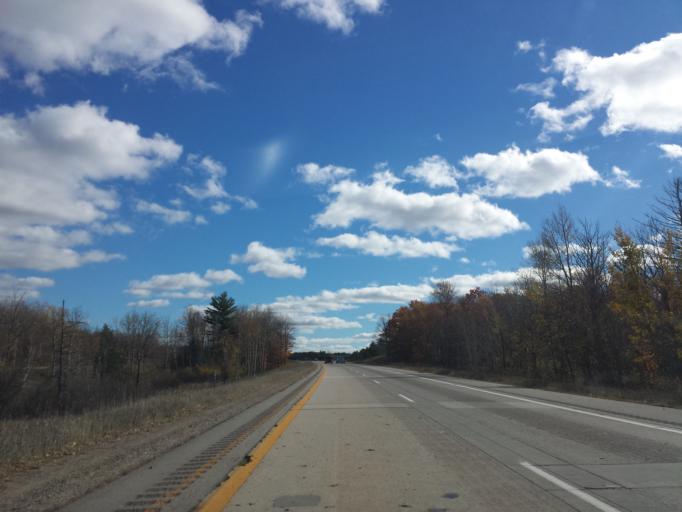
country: US
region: Michigan
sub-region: Mackinac County
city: Saint Ignace
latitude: 45.7018
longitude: -84.7219
